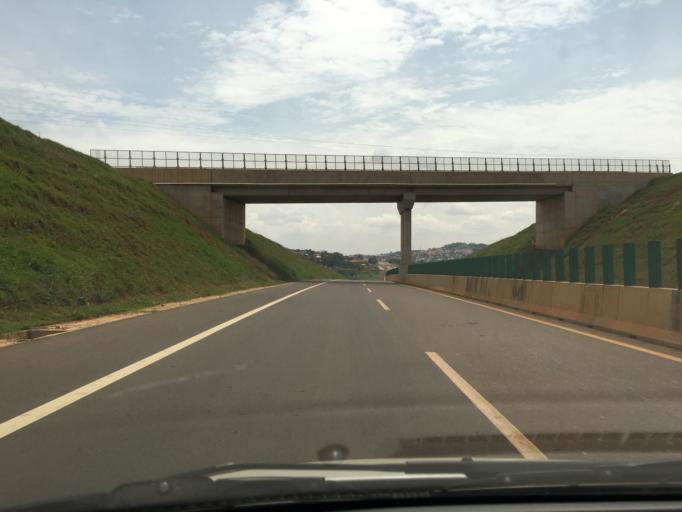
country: UG
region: Central Region
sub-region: Wakiso District
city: Kajansi
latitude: 0.1755
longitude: 32.5169
